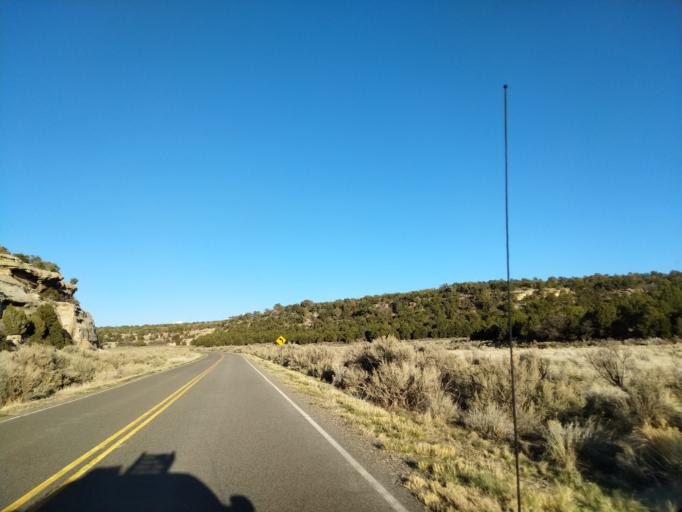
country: US
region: Colorado
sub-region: Mesa County
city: Redlands
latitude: 38.9886
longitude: -108.7827
